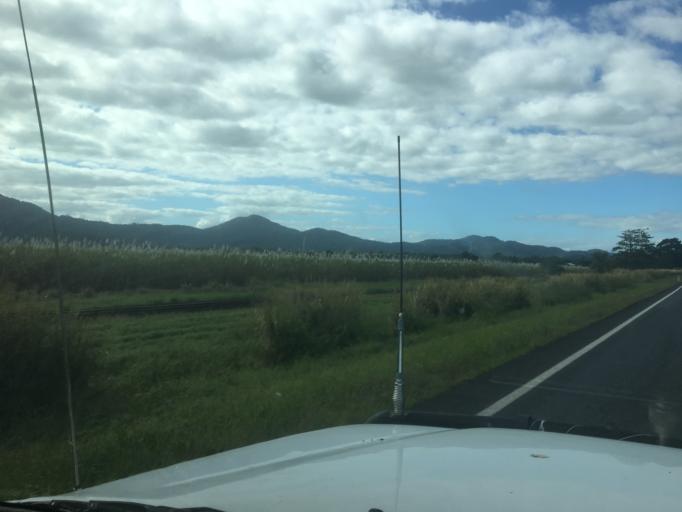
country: AU
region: Queensland
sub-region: Cassowary Coast
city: Innisfail
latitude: -17.2916
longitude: 145.9258
